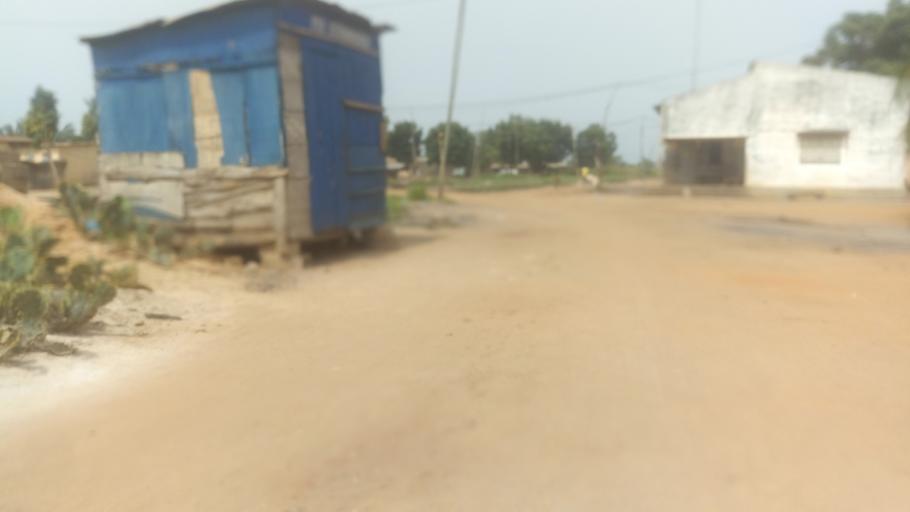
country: TG
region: Maritime
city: Lome
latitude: 6.2805
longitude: 1.2094
